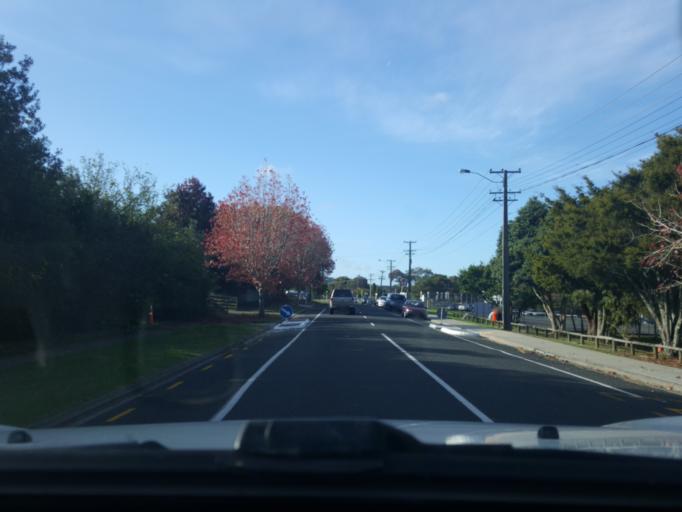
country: NZ
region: Auckland
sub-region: Auckland
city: Rosebank
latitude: -36.7600
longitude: 174.5898
